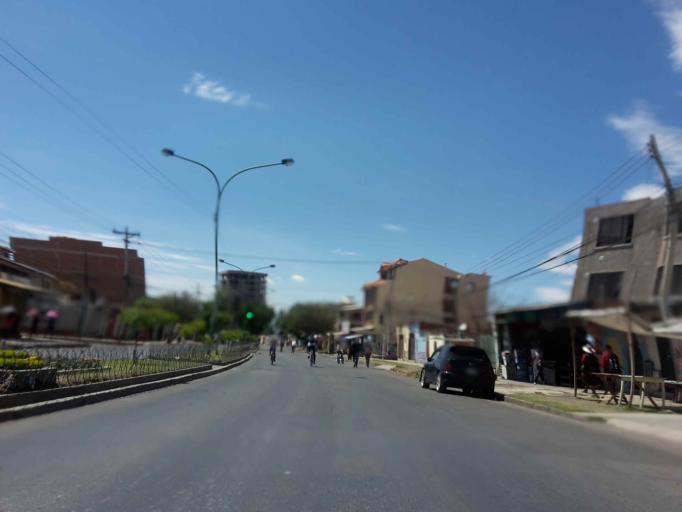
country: BO
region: Cochabamba
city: Cochabamba
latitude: -17.3628
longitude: -66.1811
